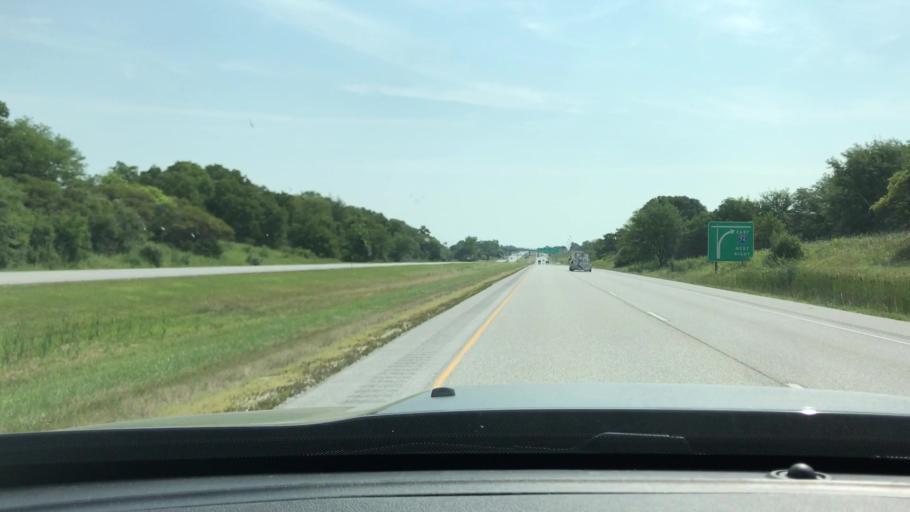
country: US
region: Illinois
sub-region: Henry County
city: Green Rock
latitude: 41.4405
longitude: -90.3441
